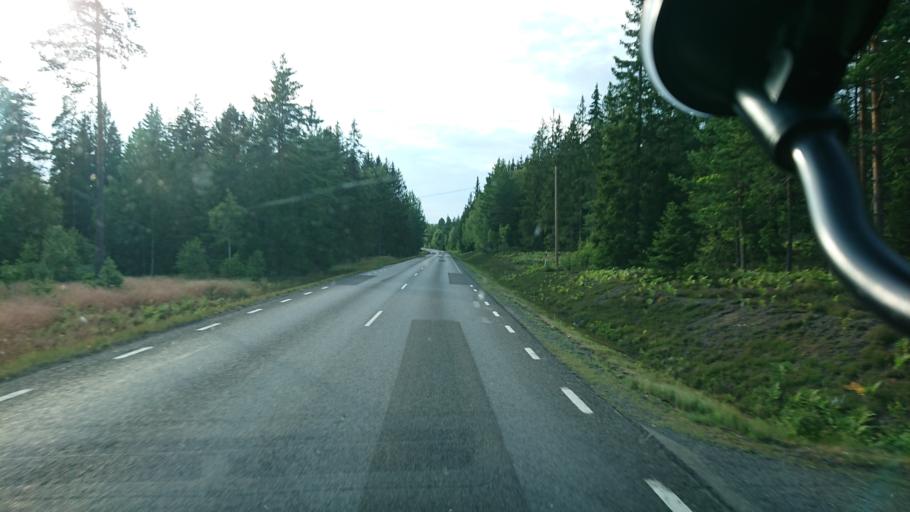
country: SE
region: Kronoberg
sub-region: Vaxjo Kommun
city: Rottne
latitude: 57.0278
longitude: 14.9776
